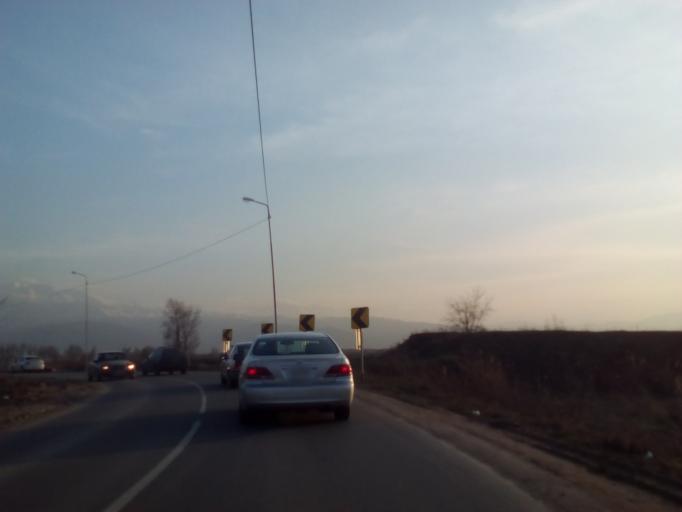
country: KZ
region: Almaty Oblysy
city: Burunday
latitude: 43.2343
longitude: 76.7407
